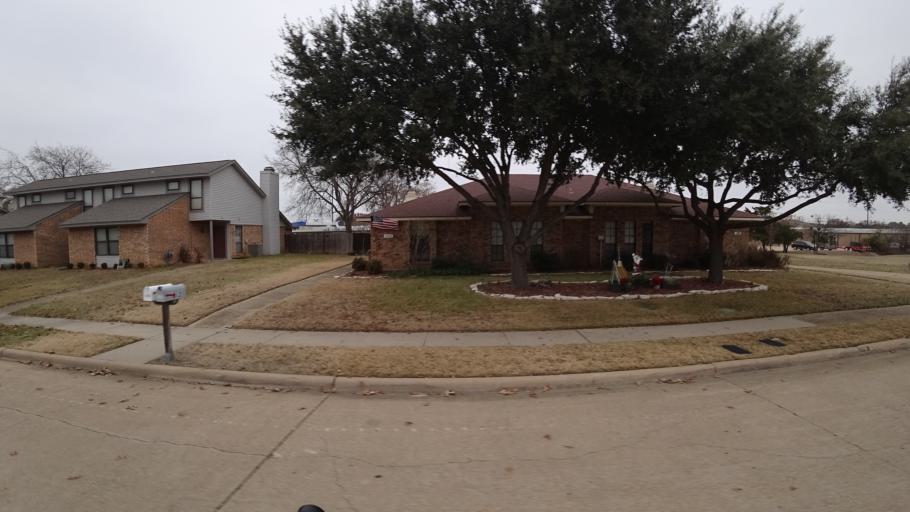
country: US
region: Texas
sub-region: Denton County
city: Highland Village
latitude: 33.0561
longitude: -97.0371
